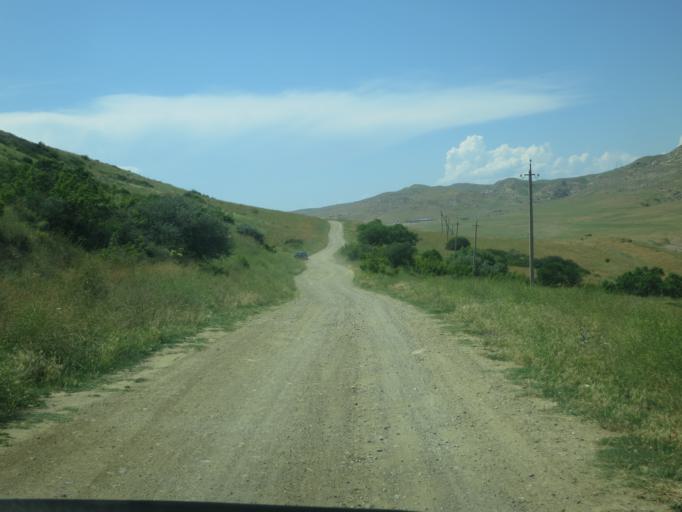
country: AZ
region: Agstafa
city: Saloglu
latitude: 41.4505
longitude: 45.3744
